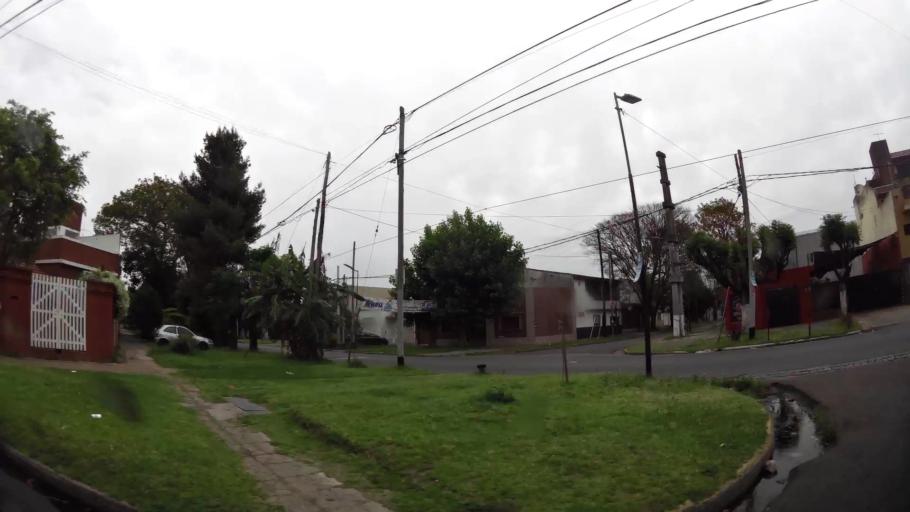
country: AR
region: Buenos Aires
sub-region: Partido de Lanus
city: Lanus
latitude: -34.6999
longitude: -58.3994
